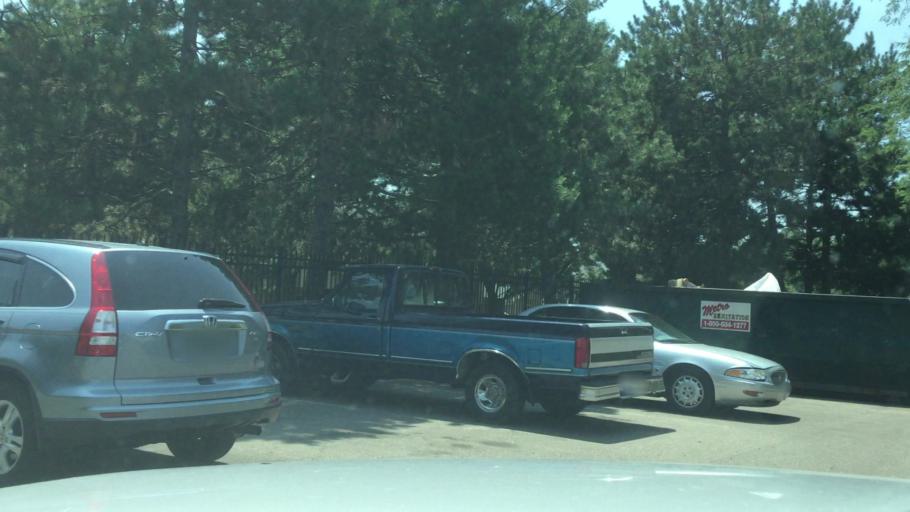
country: US
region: Michigan
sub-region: Wayne County
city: Detroit
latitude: 42.3451
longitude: -83.0214
